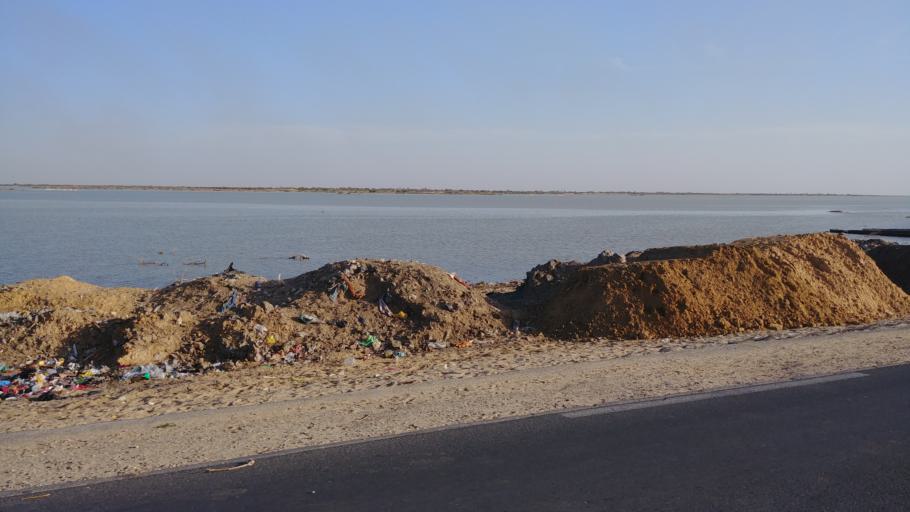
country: SN
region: Saint-Louis
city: Saint-Louis
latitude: 16.0234
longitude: -16.4826
